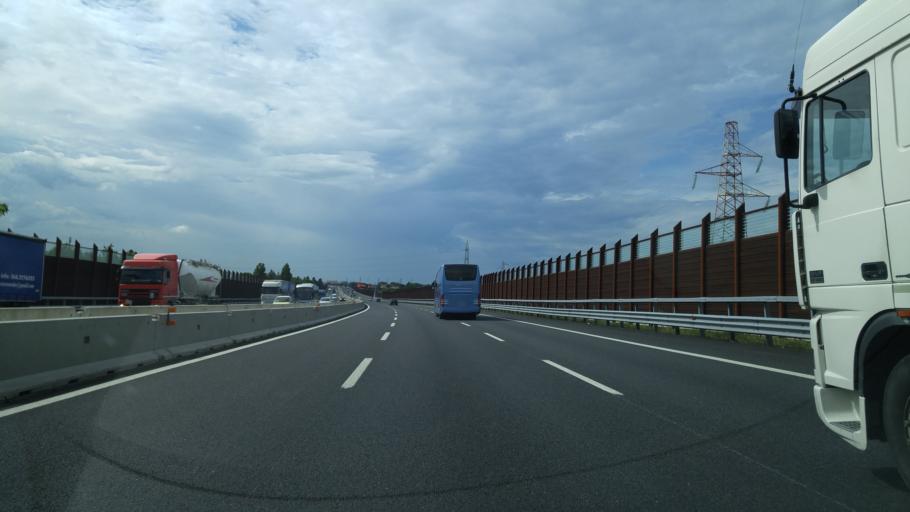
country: IT
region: Emilia-Romagna
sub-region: Provincia di Rimini
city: Rivazzurra
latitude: 44.0248
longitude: 12.5816
